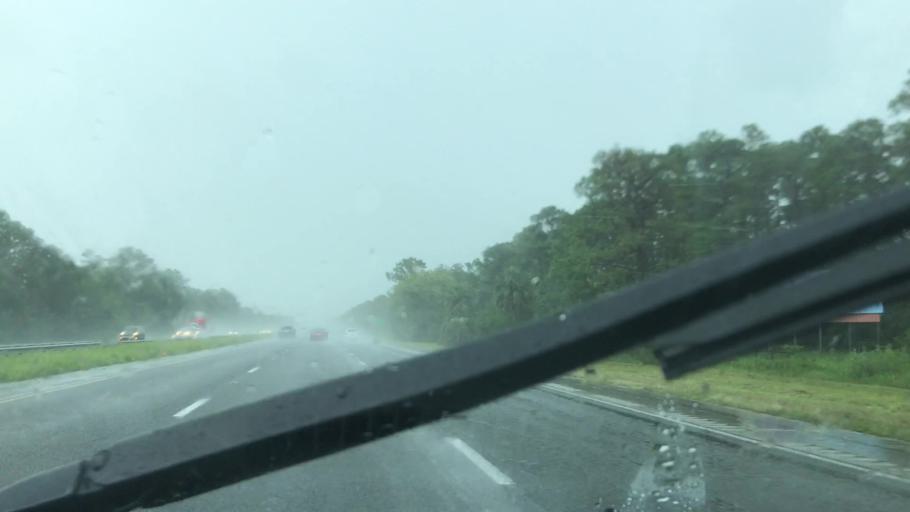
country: US
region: Florida
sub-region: Flagler County
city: Flagler Beach
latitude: 29.3913
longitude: -81.1499
